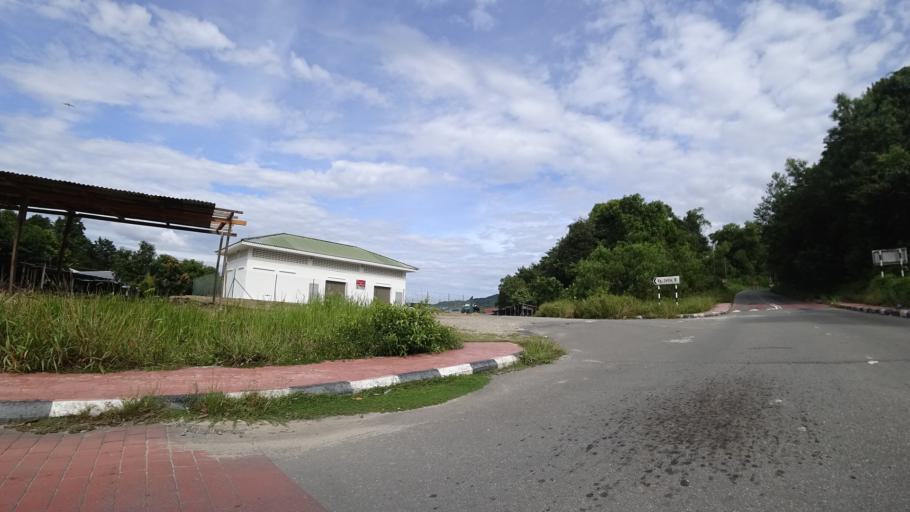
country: BN
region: Brunei and Muara
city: Bandar Seri Begawan
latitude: 4.8645
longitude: 114.9455
